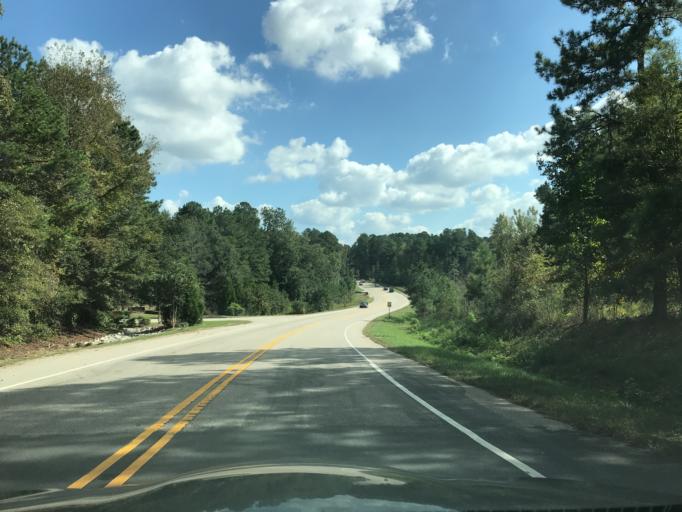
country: US
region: North Carolina
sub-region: Wake County
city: Wake Forest
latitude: 35.9108
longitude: -78.5285
